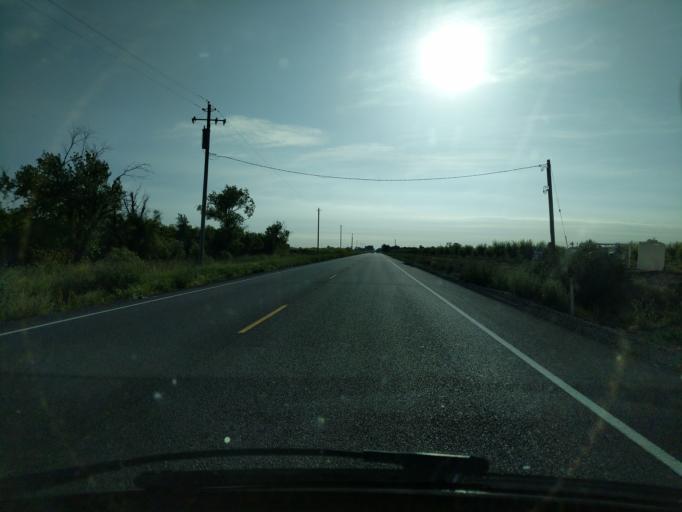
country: US
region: California
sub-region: San Joaquin County
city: Escalon
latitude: 37.9303
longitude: -120.9694
